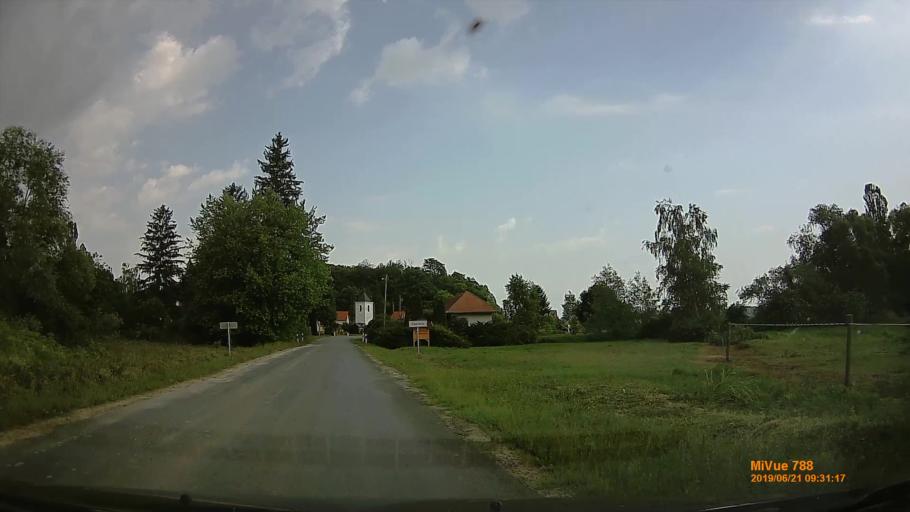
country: HU
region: Somogy
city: Taszar
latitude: 46.3044
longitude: 17.8814
